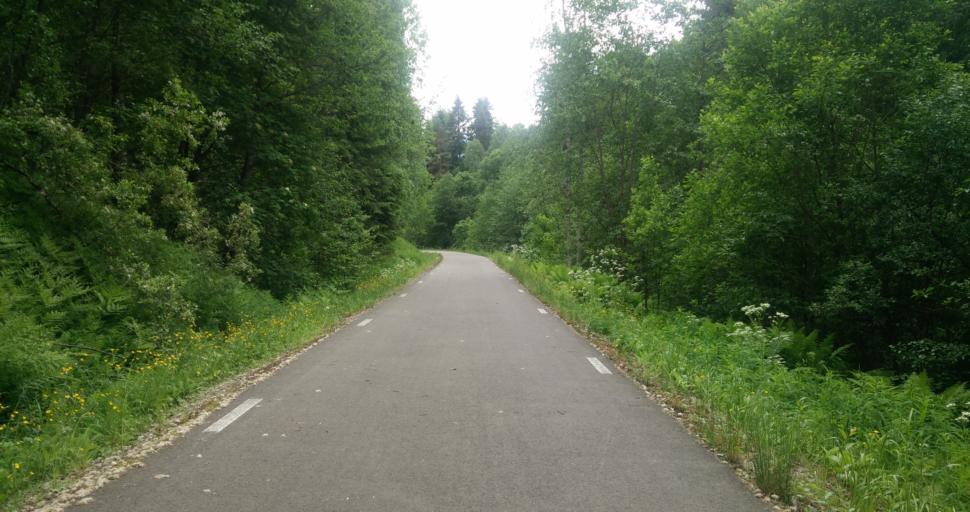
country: SE
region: Vaermland
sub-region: Hagfors Kommun
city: Hagfors
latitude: 59.9909
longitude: 13.5870
